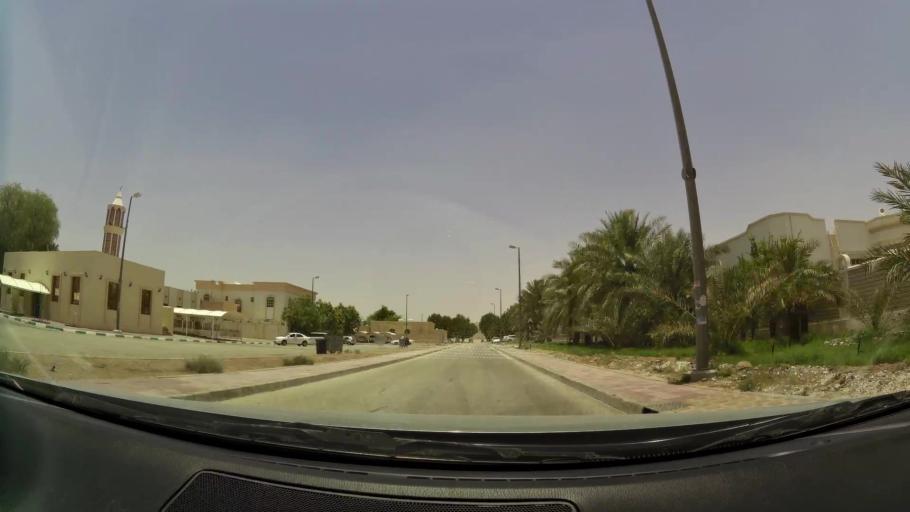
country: OM
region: Al Buraimi
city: Al Buraymi
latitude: 24.2637
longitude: 55.7345
